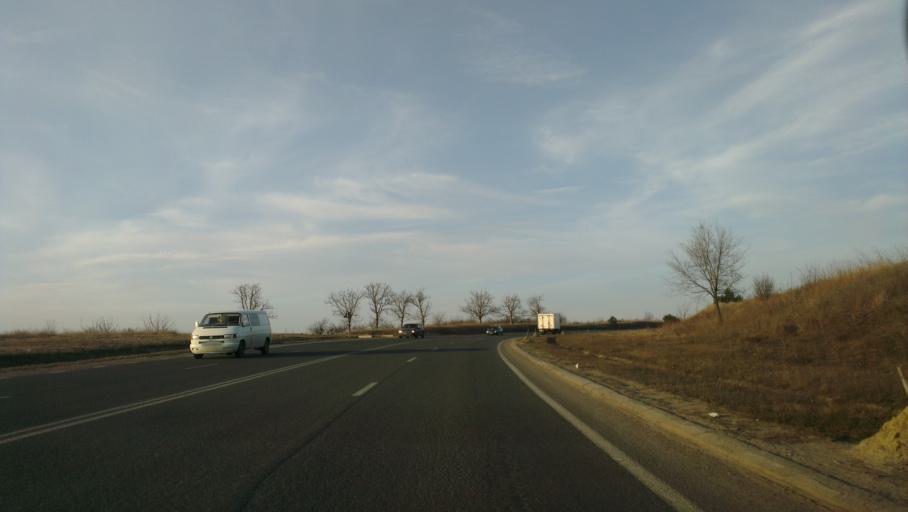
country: MD
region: Laloveni
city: Ialoveni
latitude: 46.9199
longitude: 28.6917
